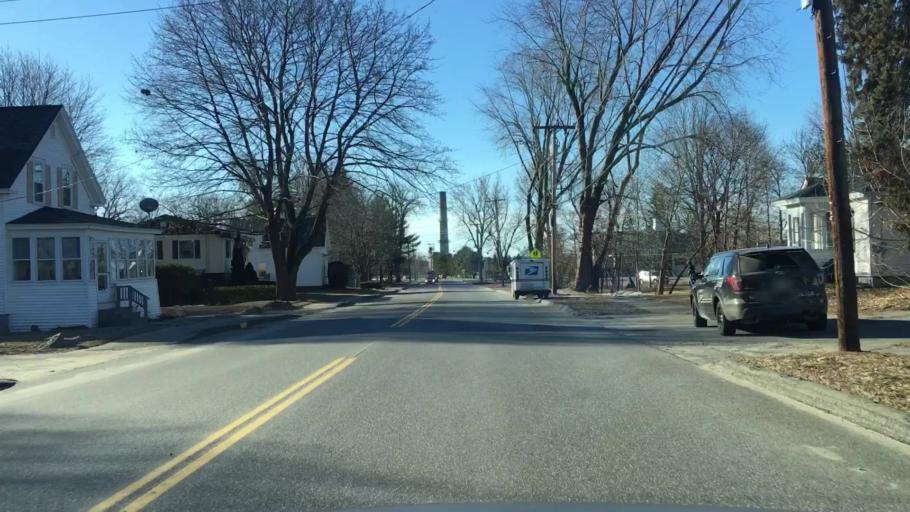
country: US
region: Maine
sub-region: Kennebec County
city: Winslow
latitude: 44.5582
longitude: -69.6179
